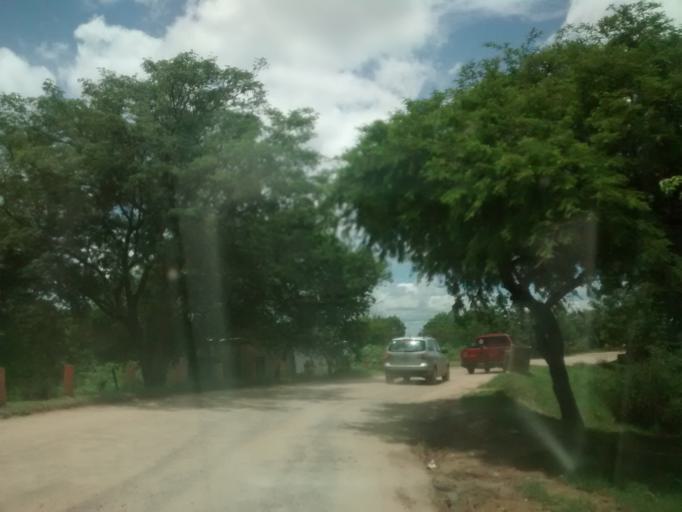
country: AR
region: Chaco
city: Fontana
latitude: -27.4261
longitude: -59.0048
